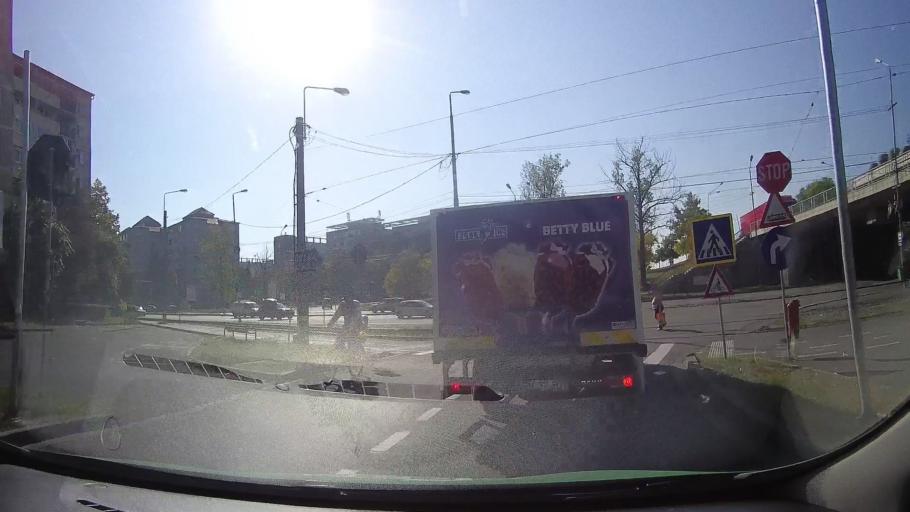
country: RO
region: Bihor
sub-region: Comuna Biharea
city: Oradea
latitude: 47.0747
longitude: 21.9080
